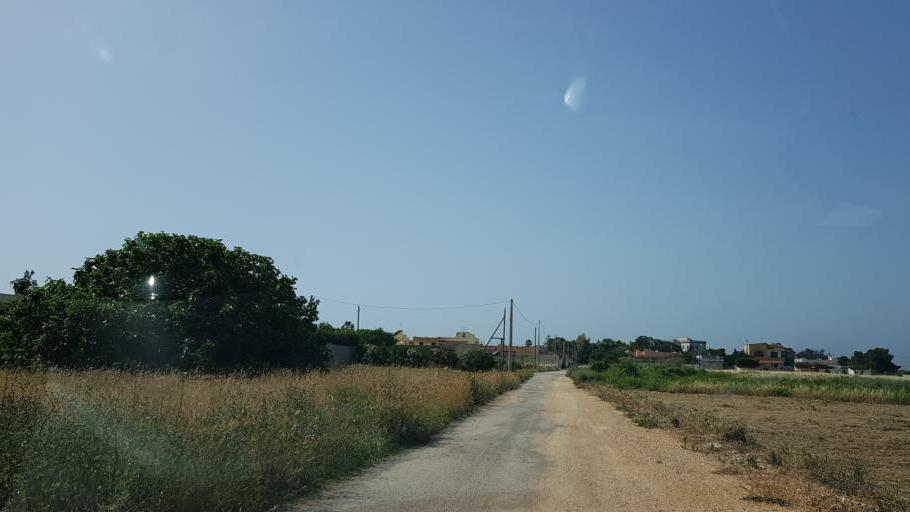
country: IT
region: Apulia
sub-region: Provincia di Brindisi
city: Materdomini
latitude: 40.6696
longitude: 17.9420
